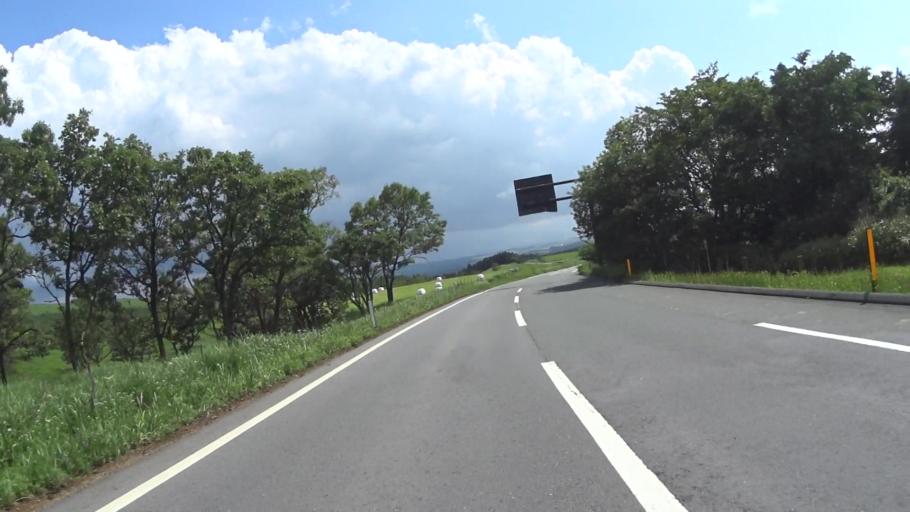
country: JP
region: Kumamoto
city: Aso
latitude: 33.0695
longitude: 131.1879
